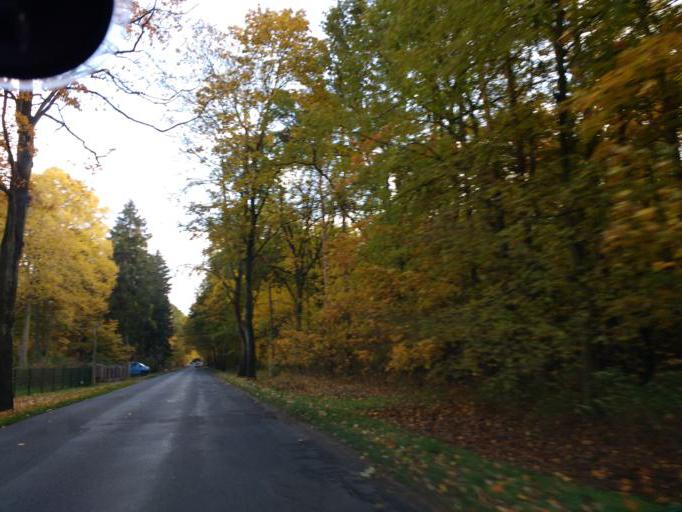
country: DE
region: Brandenburg
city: Petershagen
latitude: 52.5547
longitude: 13.8340
